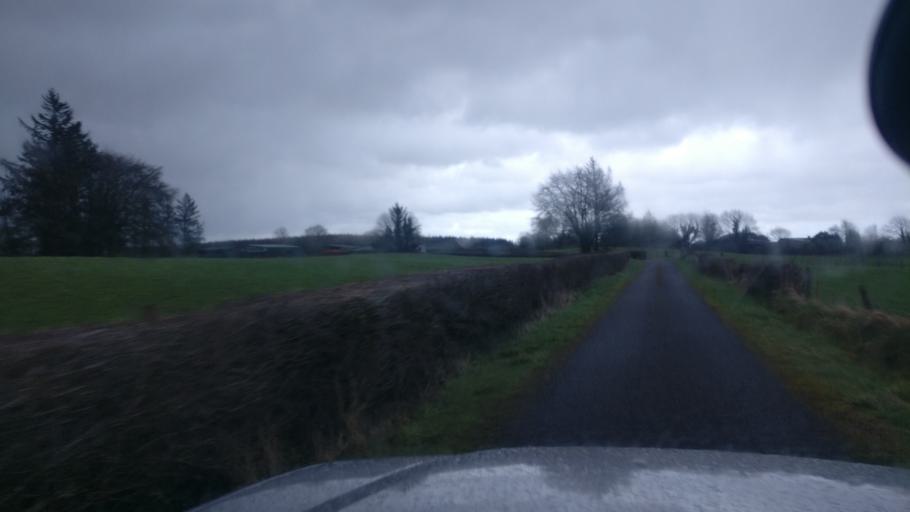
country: IE
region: Connaught
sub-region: County Galway
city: Loughrea
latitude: 53.2471
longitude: -8.4314
